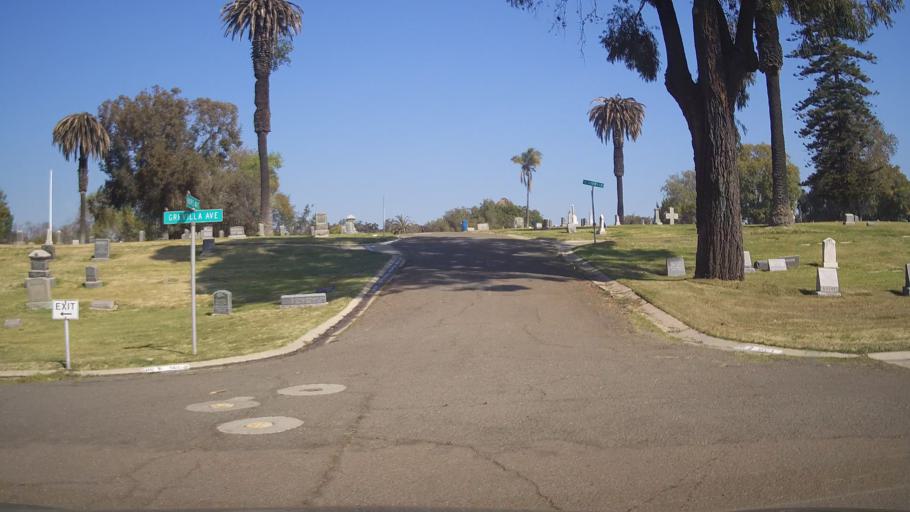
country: US
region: California
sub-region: San Diego County
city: National City
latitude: 32.7065
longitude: -117.1116
